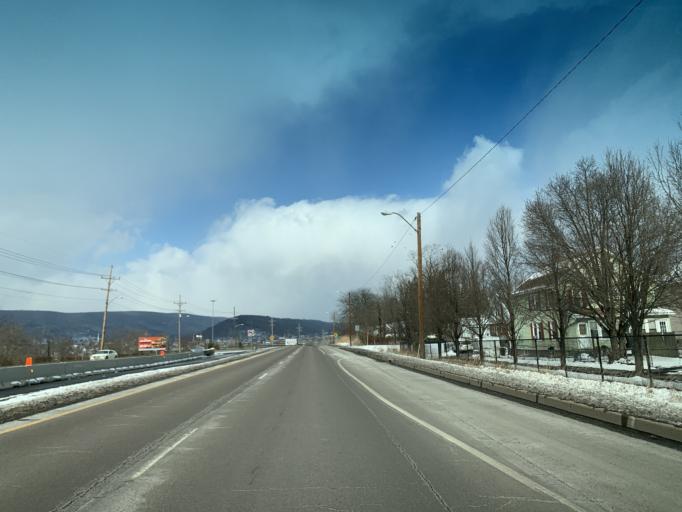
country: US
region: Maryland
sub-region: Allegany County
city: Cumberland
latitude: 39.6378
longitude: -78.7664
